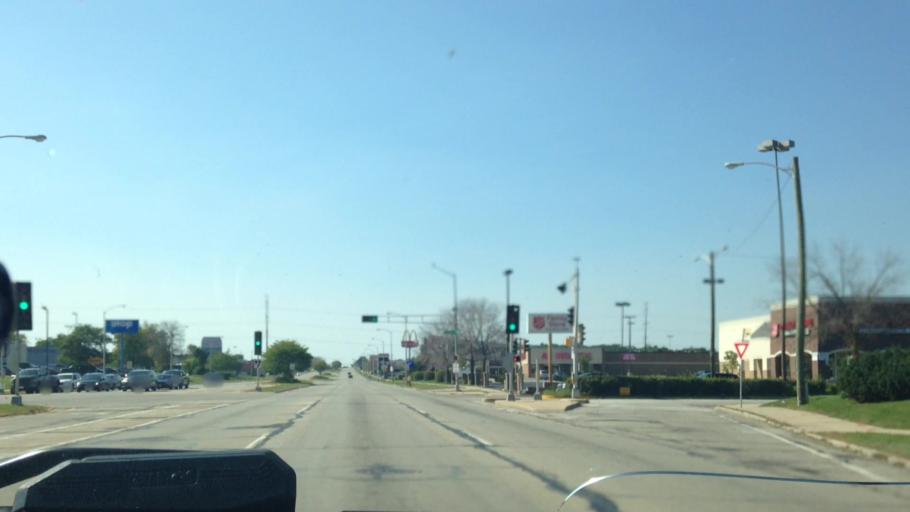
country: US
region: Wisconsin
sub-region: Milwaukee County
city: Brown Deer
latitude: 43.1779
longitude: -88.0083
